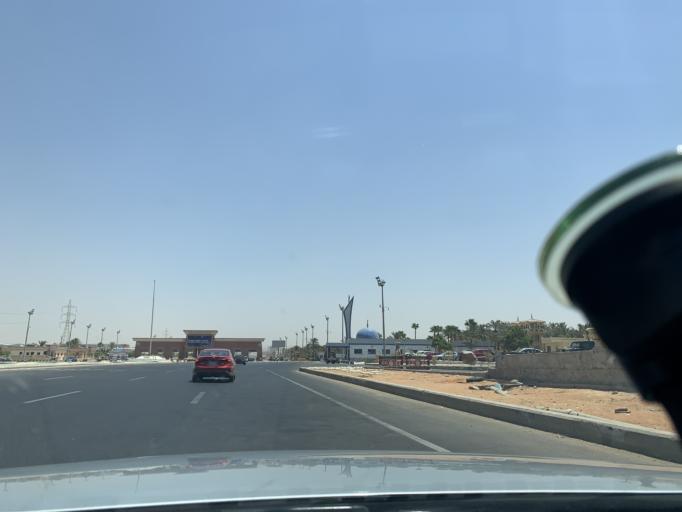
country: EG
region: Muhafazat al Qahirah
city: Halwan
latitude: 29.9640
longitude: 31.4777
